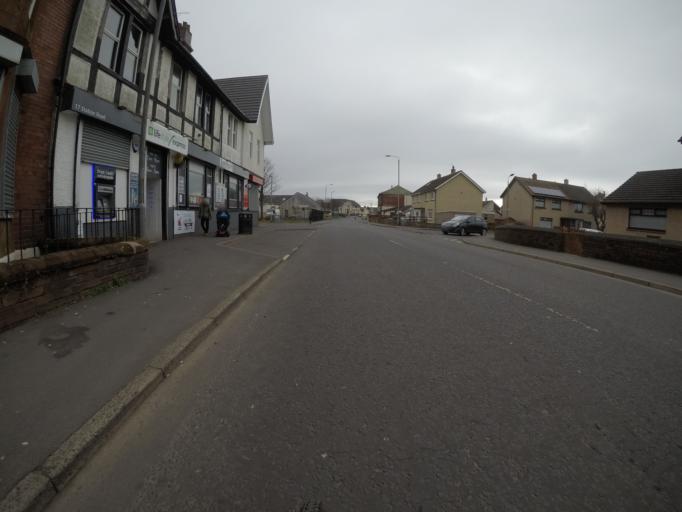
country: GB
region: Scotland
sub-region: North Ayrshire
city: Stevenston
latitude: 55.6356
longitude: -4.7527
